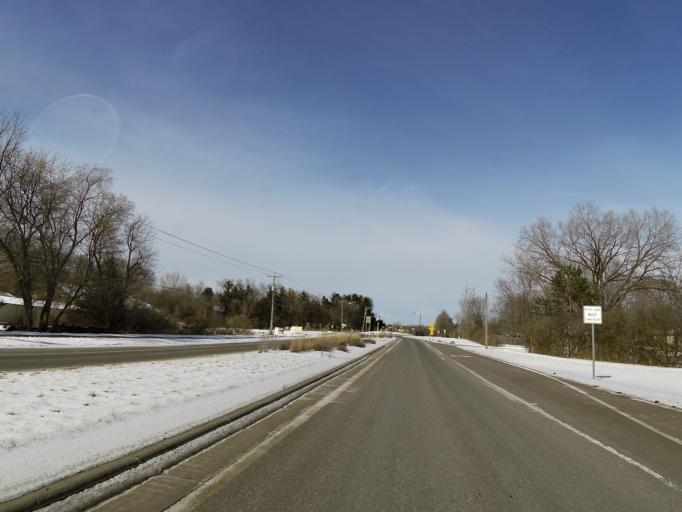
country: US
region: Minnesota
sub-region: Washington County
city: Lakeland
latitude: 44.9533
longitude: -92.7708
